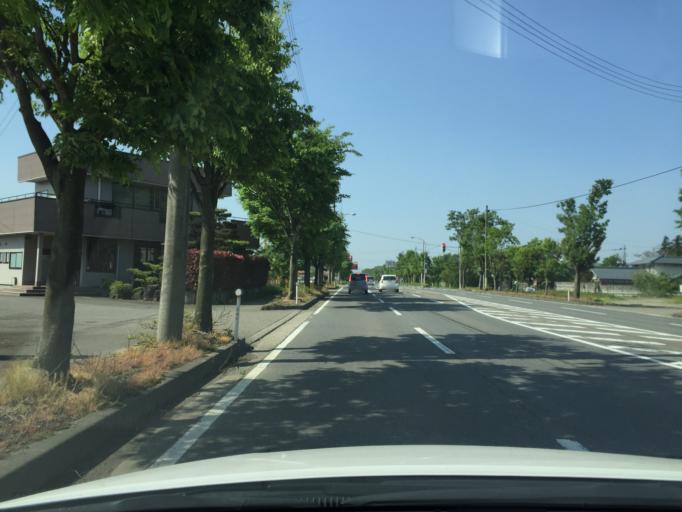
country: JP
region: Niigata
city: Gosen
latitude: 37.7638
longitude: 139.2345
